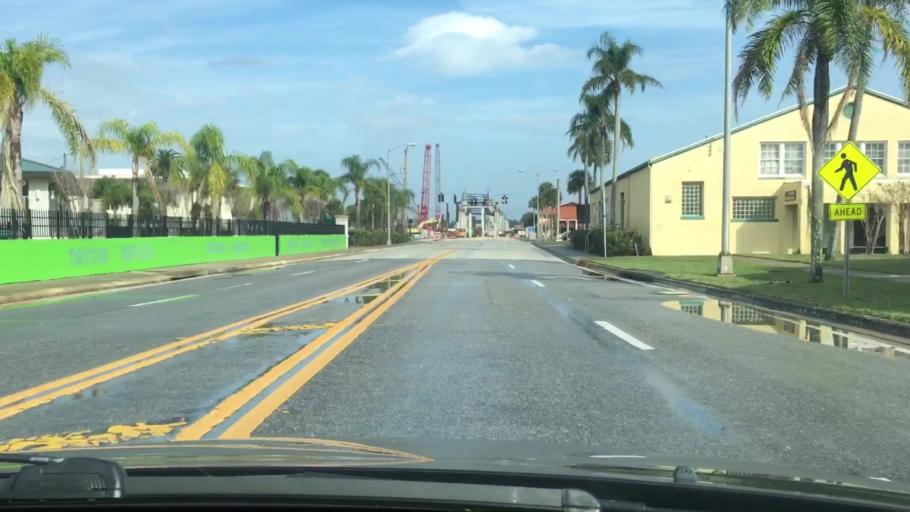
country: US
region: Florida
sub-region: Volusia County
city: Daytona Beach
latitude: 29.2091
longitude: -81.0157
